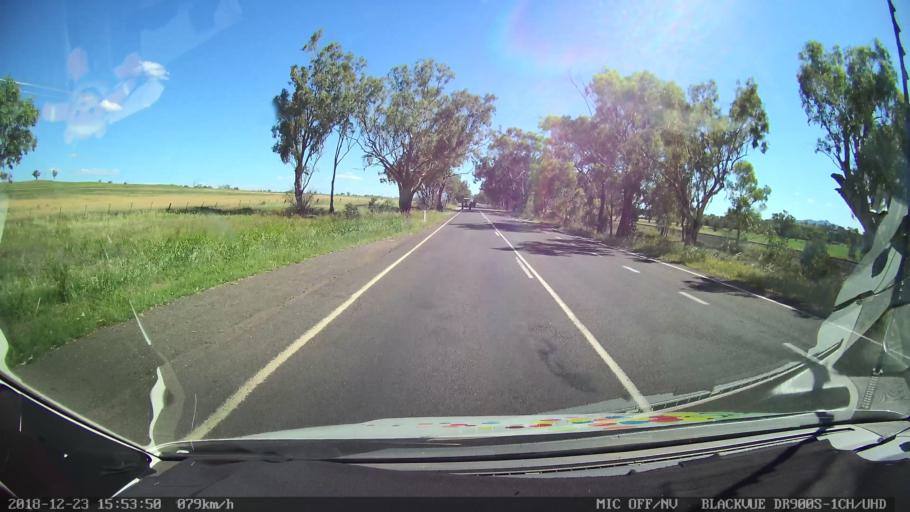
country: AU
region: New South Wales
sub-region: Tamworth Municipality
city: Phillip
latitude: -31.1382
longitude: 150.8791
